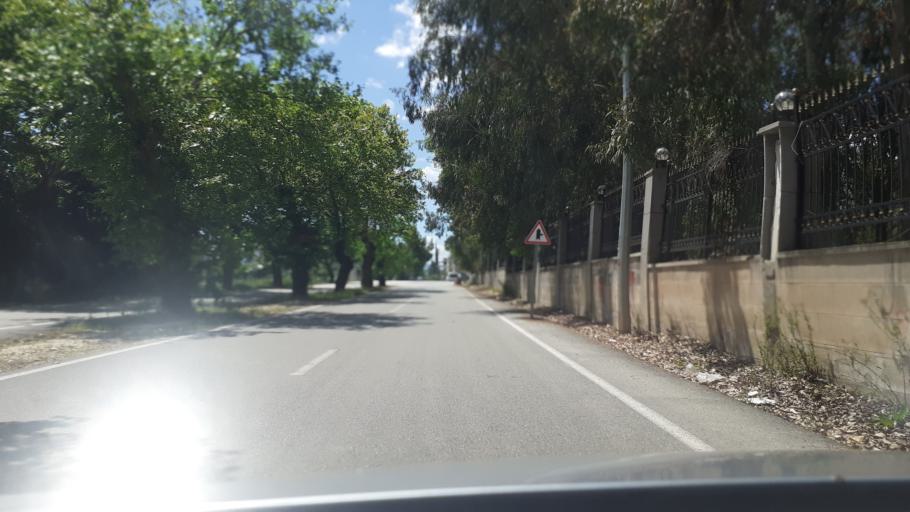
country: TR
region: Hatay
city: Anayazi
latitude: 36.3227
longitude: 36.1979
